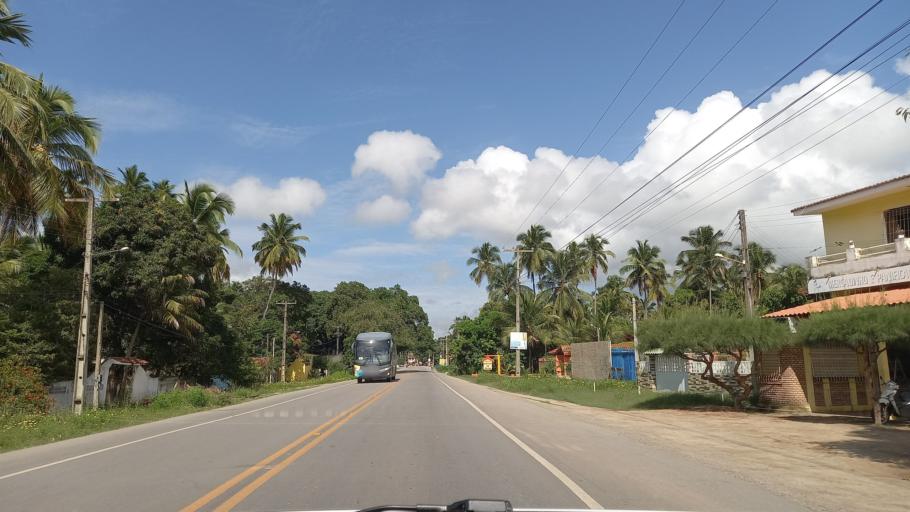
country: BR
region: Pernambuco
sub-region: Sao Jose Da Coroa Grande
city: Sao Jose da Coroa Grande
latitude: -8.9287
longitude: -35.1644
